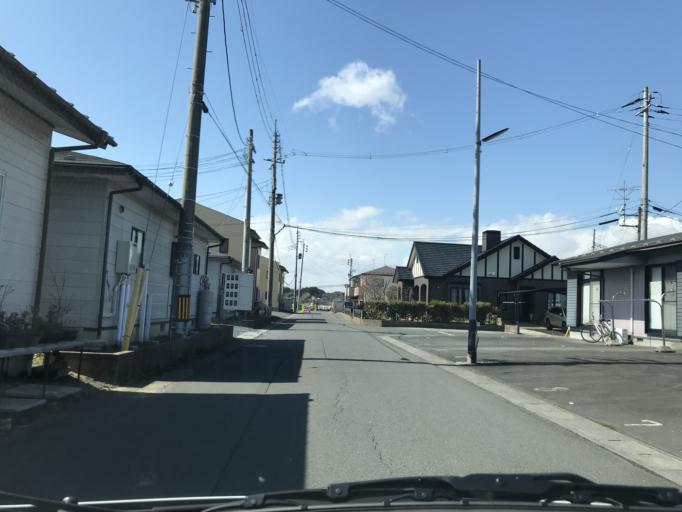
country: JP
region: Miyagi
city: Wakuya
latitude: 38.6871
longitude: 141.1810
